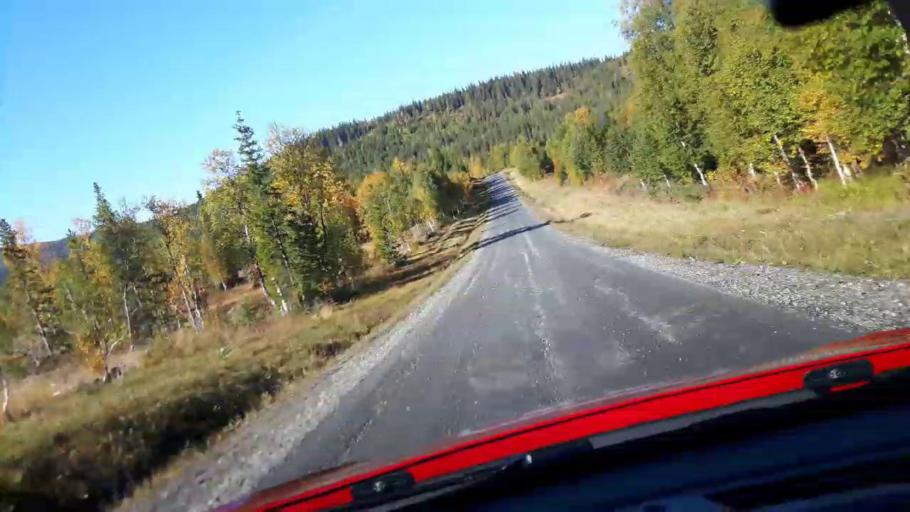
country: NO
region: Nord-Trondelag
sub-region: Lierne
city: Sandvika
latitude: 64.6107
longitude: 13.7379
